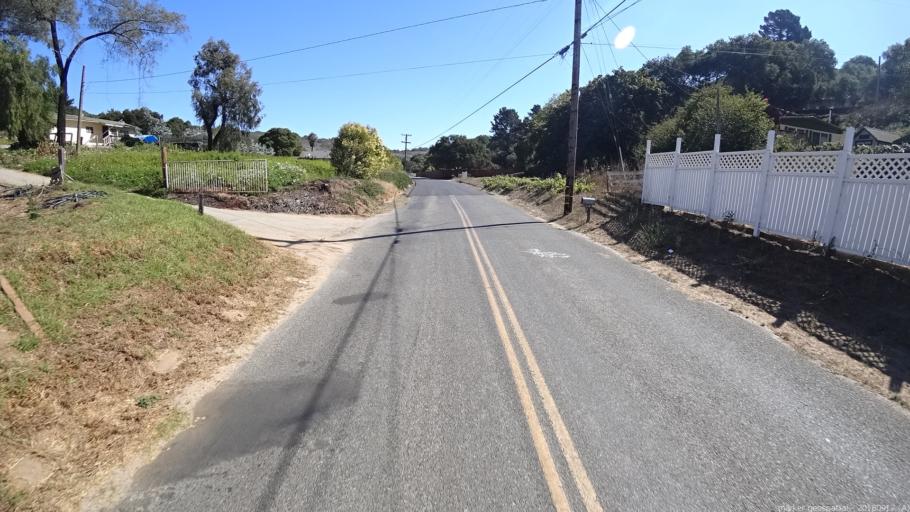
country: US
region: California
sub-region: Monterey County
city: Elkhorn
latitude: 36.8307
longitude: -121.6990
